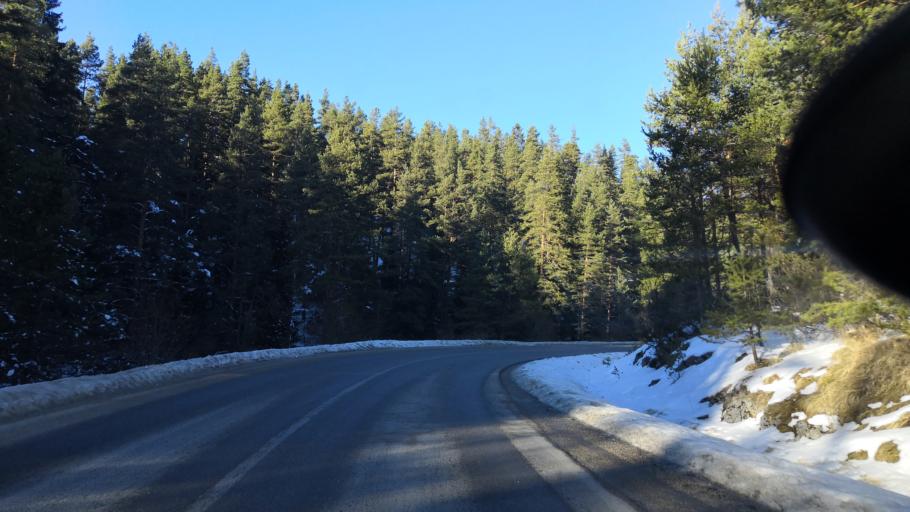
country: BA
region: Republika Srpska
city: Sokolac
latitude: 43.9830
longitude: 18.8621
